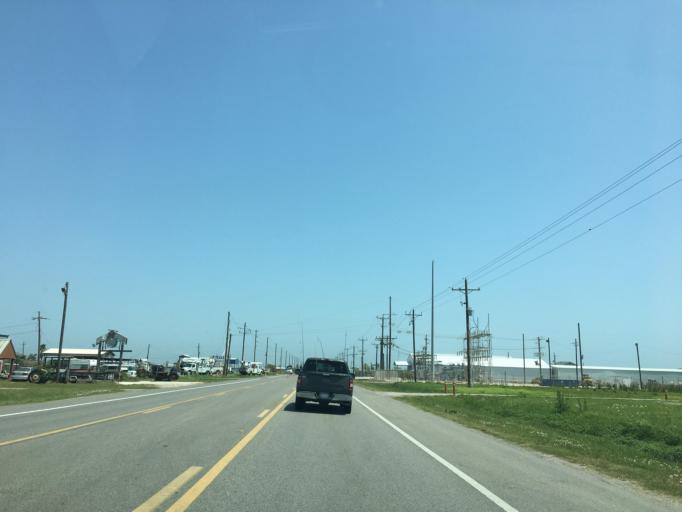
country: US
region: Texas
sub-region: Galveston County
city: Bolivar Peninsula
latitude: 29.4428
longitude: -94.6653
